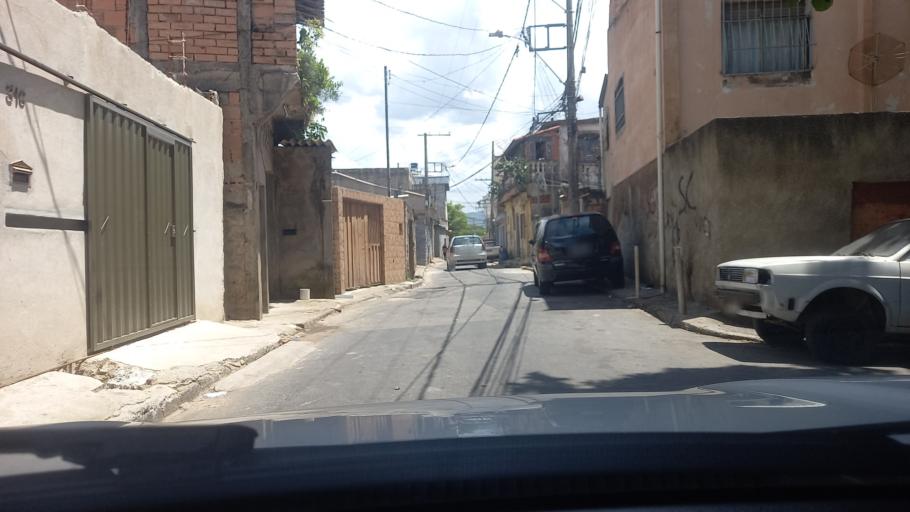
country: BR
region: Minas Gerais
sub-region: Belo Horizonte
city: Belo Horizonte
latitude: -19.9198
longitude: -43.9839
